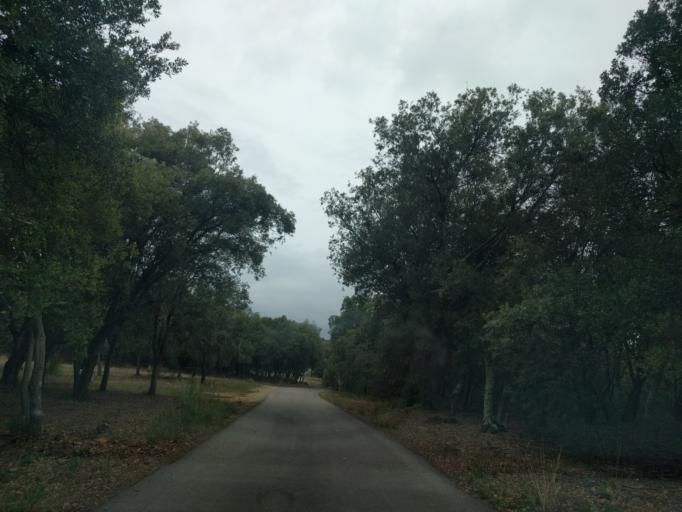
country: ES
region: Catalonia
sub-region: Provincia de Girona
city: la Cellera de Ter
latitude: 42.0238
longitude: 2.6268
